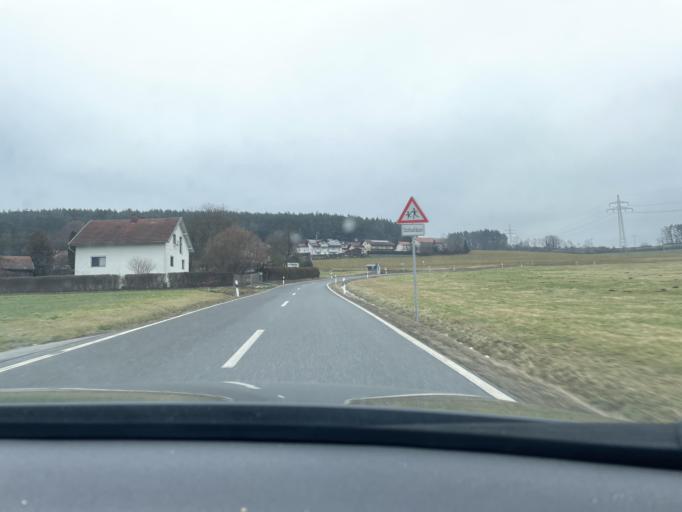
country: DE
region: Bavaria
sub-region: Upper Palatinate
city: Zandt
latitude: 49.1887
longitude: 12.6997
